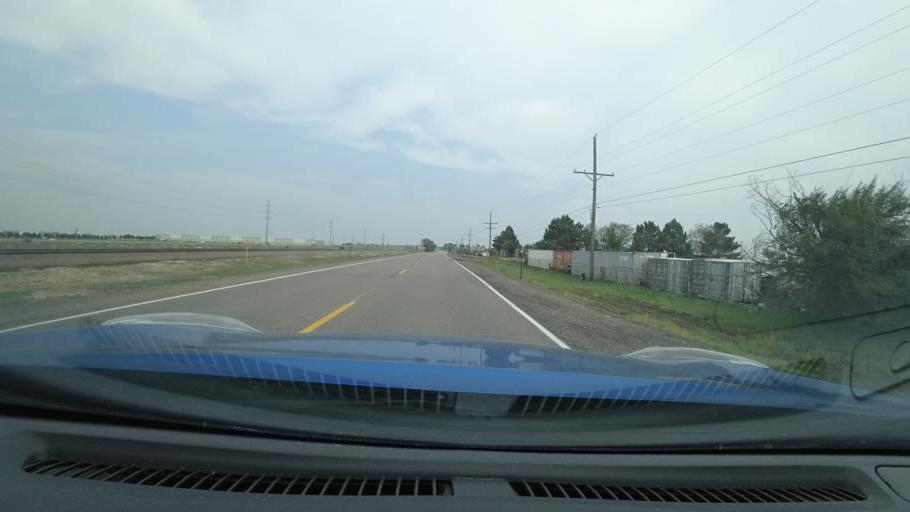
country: US
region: Colorado
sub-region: Adams County
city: Aurora
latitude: 39.7532
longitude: -104.7660
